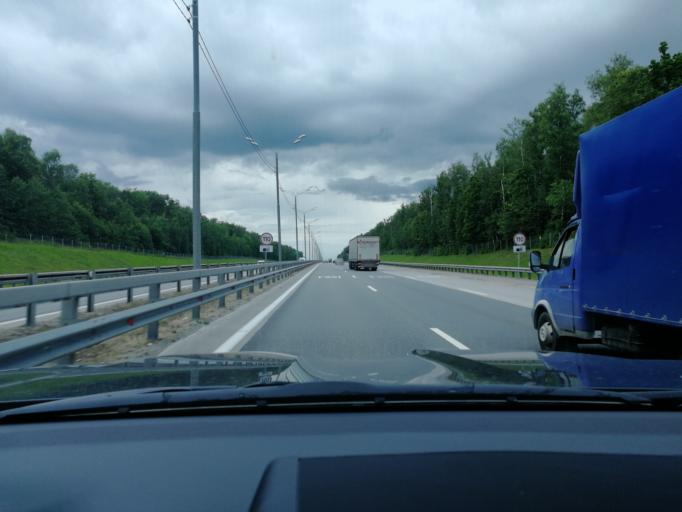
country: RU
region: Moskovskaya
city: Belyye Stolby
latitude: 55.2961
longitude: 37.8430
